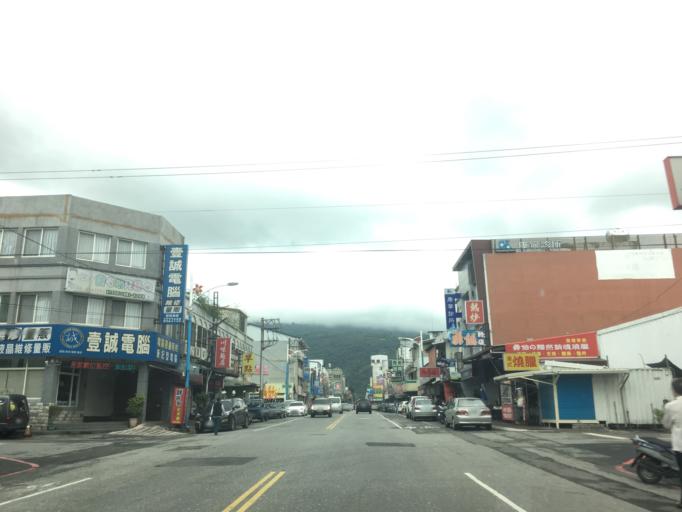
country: TW
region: Taiwan
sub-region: Hualien
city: Hualian
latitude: 23.9787
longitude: 121.5691
